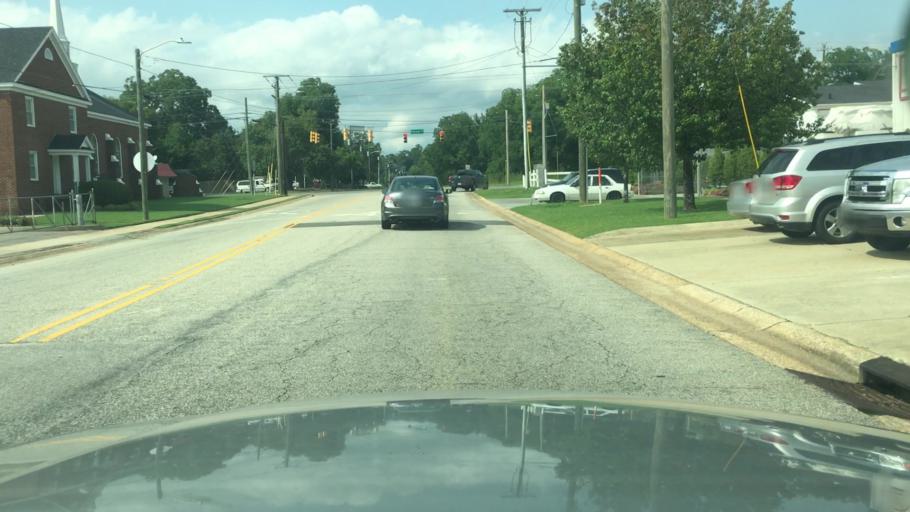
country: US
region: North Carolina
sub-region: Cumberland County
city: Fayetteville
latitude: 35.0467
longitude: -78.8612
